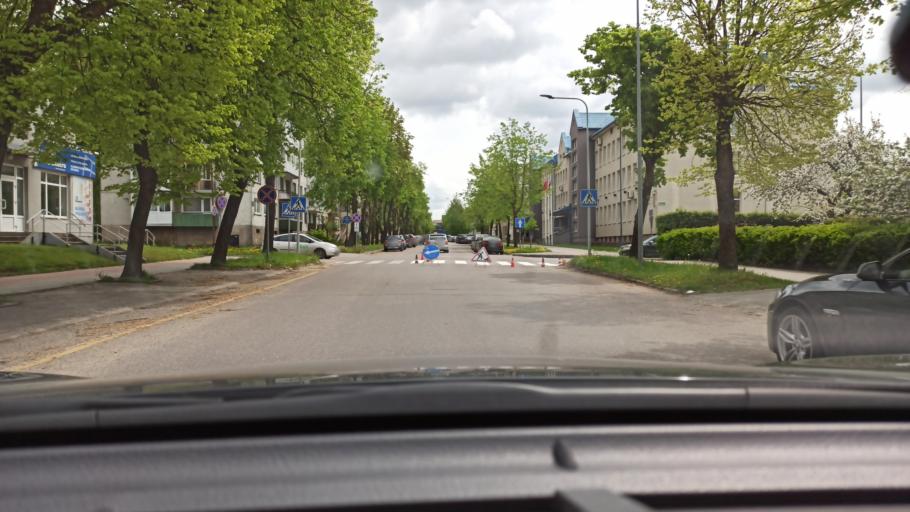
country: LT
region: Siauliu apskritis
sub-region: Siauliai
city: Siauliai
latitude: 55.9308
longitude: 23.3037
